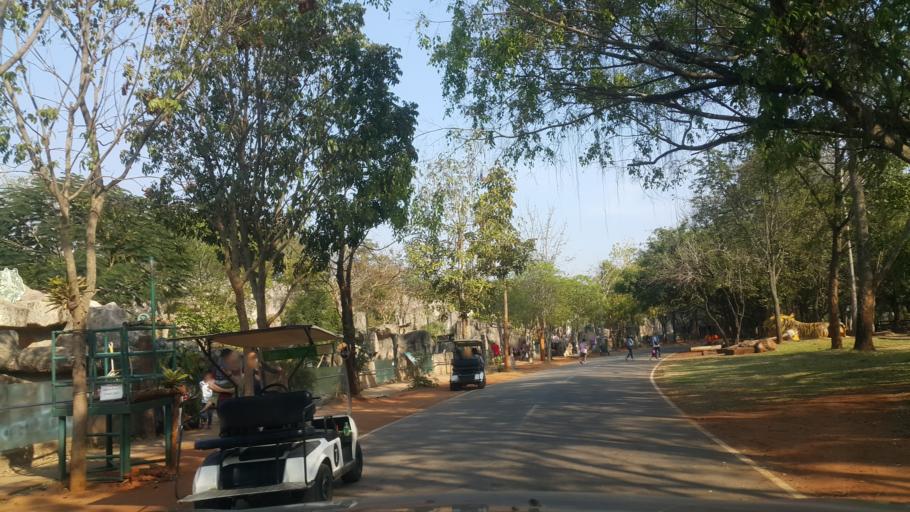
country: TH
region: Nakhon Ratchasima
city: Nakhon Ratchasima
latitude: 14.8561
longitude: 102.0879
